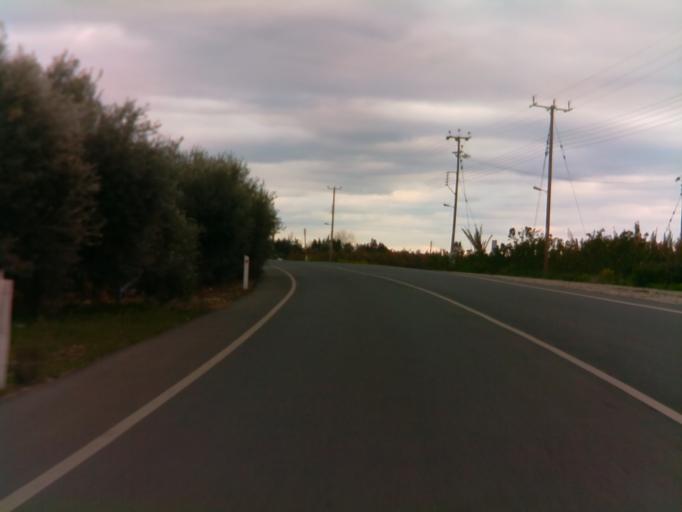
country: CY
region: Pafos
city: Pegeia
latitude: 34.8951
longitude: 32.3338
